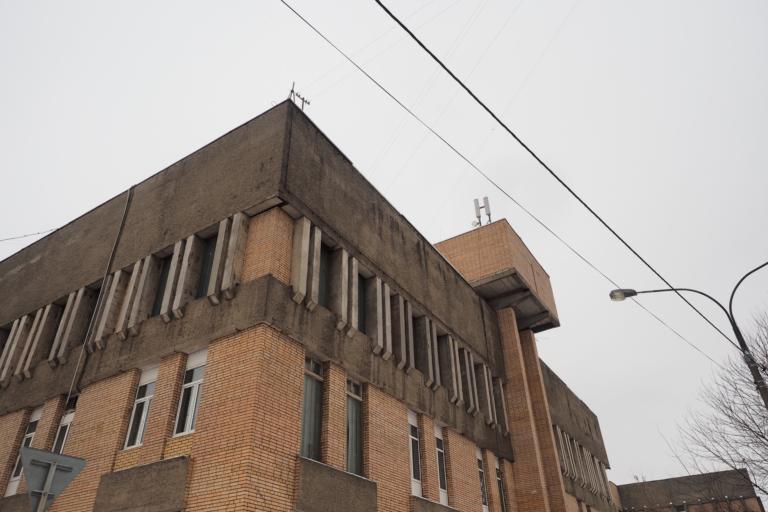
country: RU
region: Moskovskaya
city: Shchelkovo
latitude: 55.9254
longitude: 37.9934
